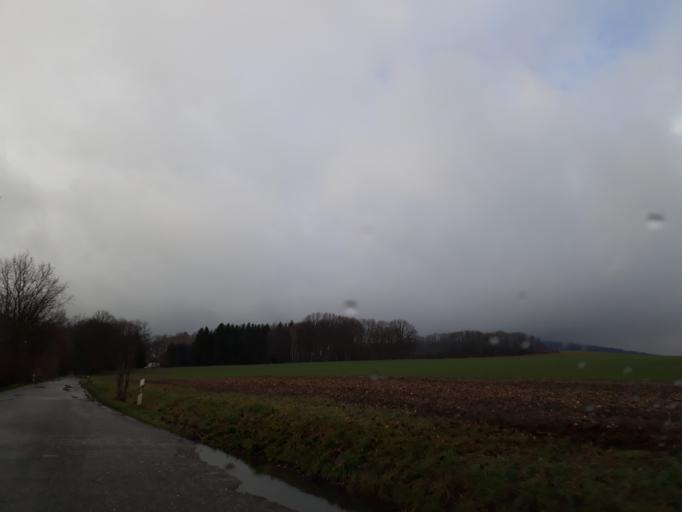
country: DE
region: Saxony
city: Eibau
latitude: 50.9883
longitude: 14.6954
